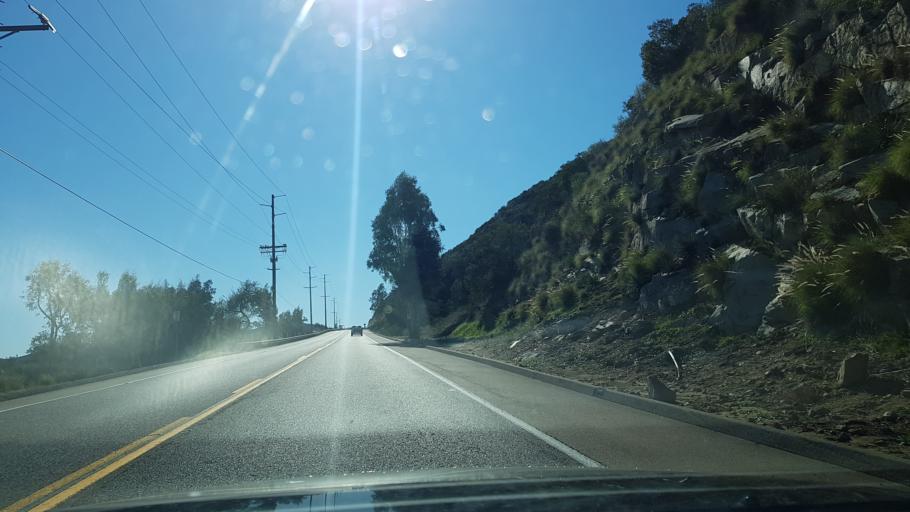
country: US
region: California
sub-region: San Diego County
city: Escondido
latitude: 33.0758
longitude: -117.1210
